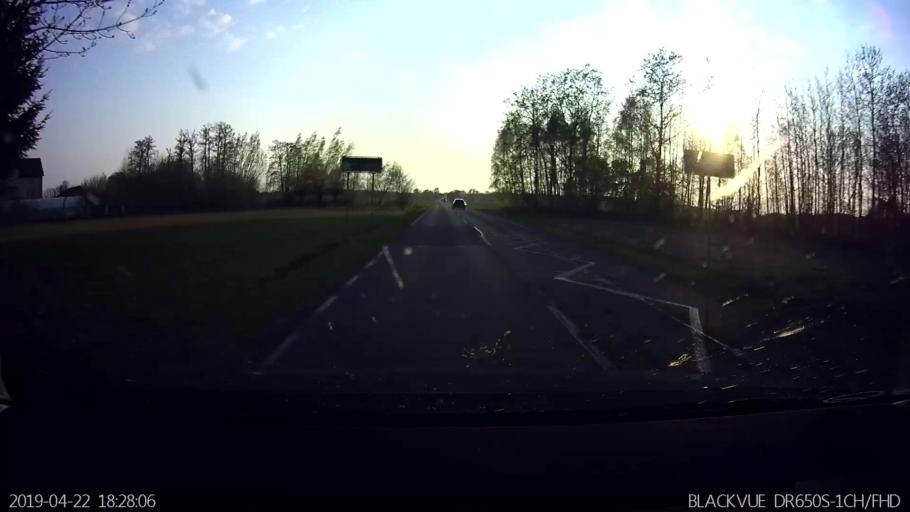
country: PL
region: Masovian Voivodeship
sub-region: Powiat wolominski
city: Tluszcz
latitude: 52.4603
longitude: 21.4814
